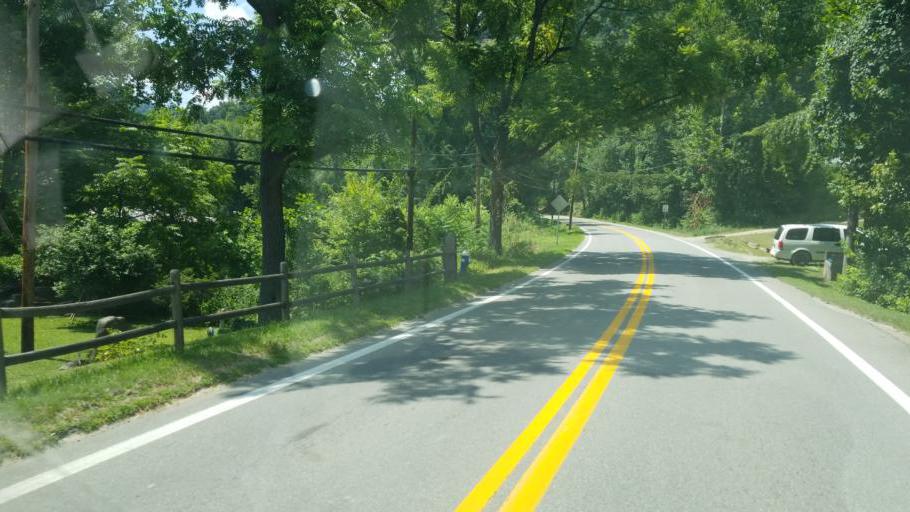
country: US
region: West Virginia
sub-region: Kanawha County
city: Chesapeake
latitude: 38.1725
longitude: -81.4460
